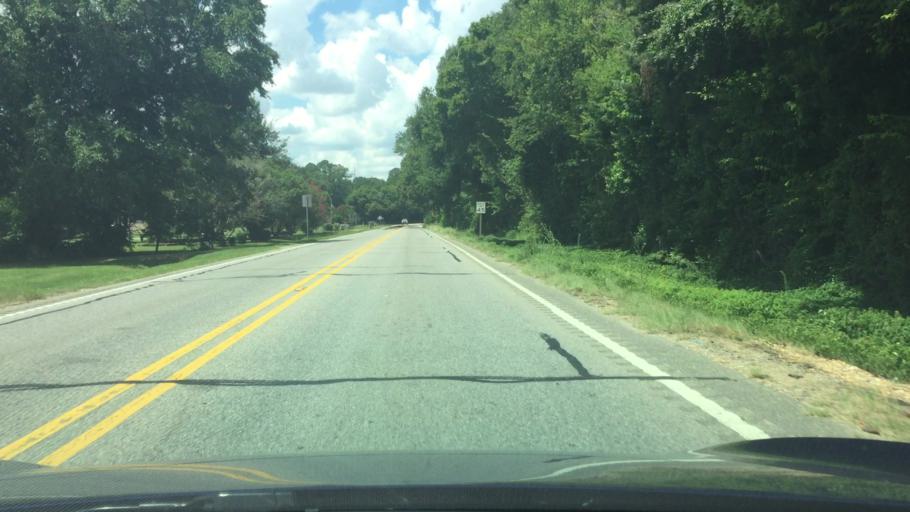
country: US
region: Alabama
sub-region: Montgomery County
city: Pike Road
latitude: 32.3666
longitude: -86.0395
